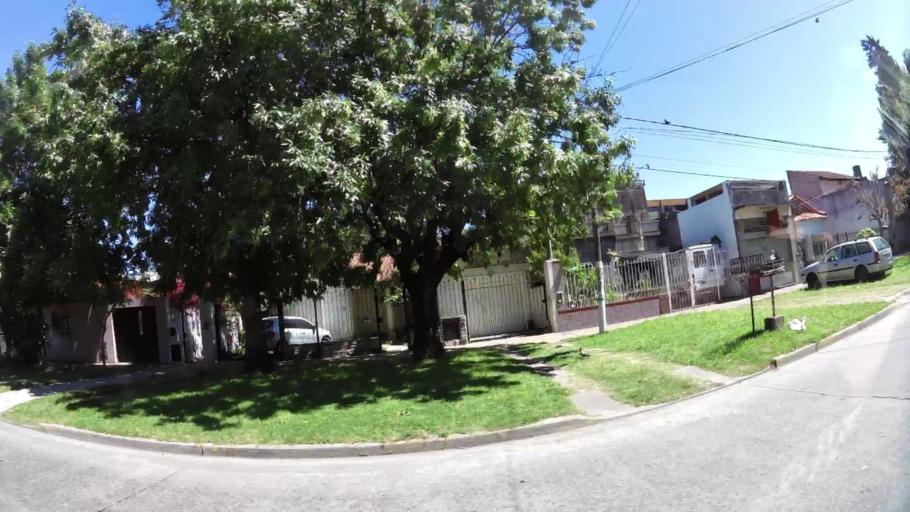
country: AR
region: Buenos Aires
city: Caseros
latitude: -34.5932
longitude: -58.5673
